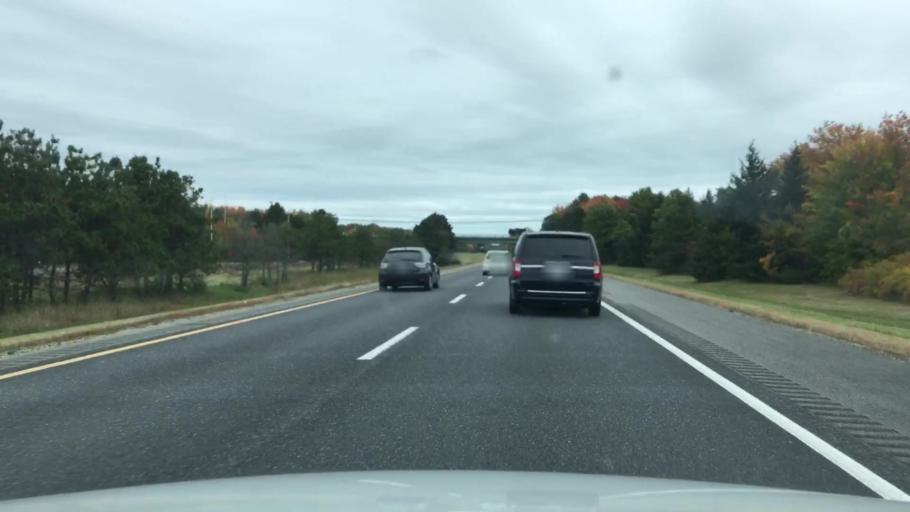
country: US
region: Maine
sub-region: Sagadahoc County
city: Topsham
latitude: 43.9400
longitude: -69.9808
